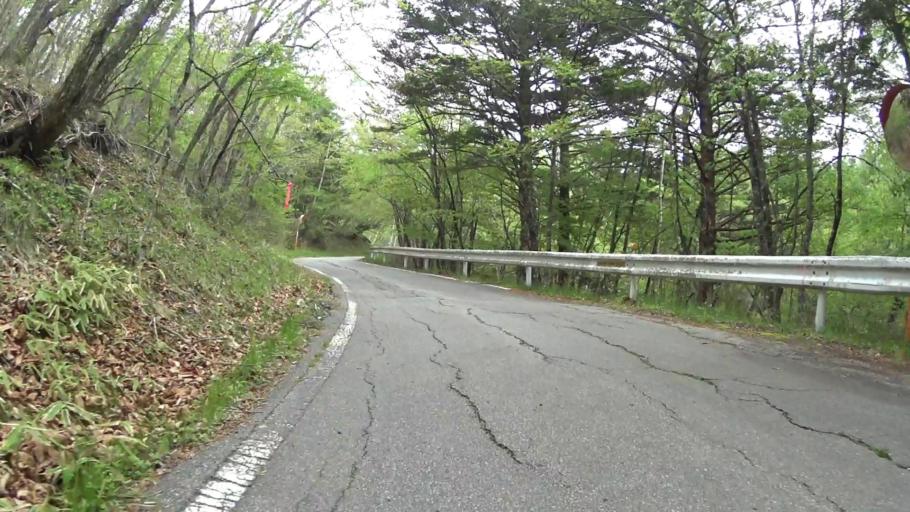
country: JP
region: Yamanashi
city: Kofu-shi
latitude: 35.8425
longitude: 138.5780
